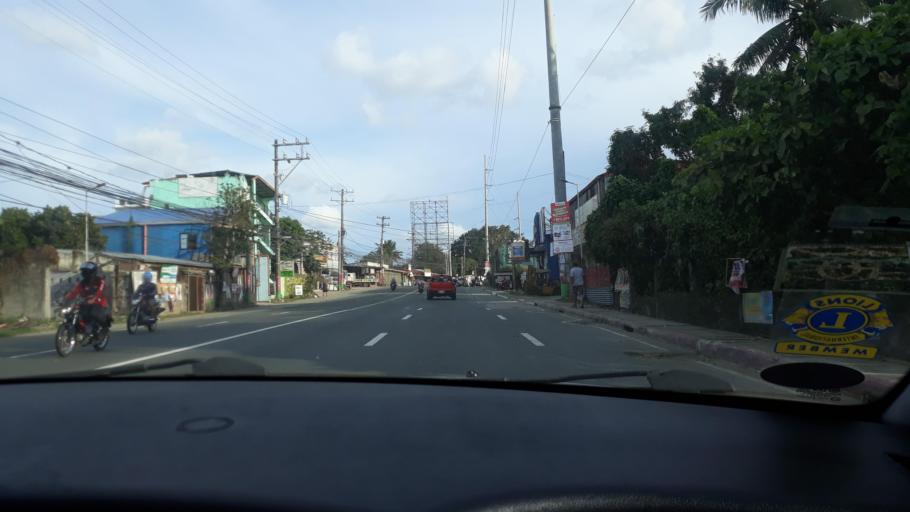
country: PH
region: Calabarzon
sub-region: Province of Cavite
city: Biga
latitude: 14.2551
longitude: 120.9742
